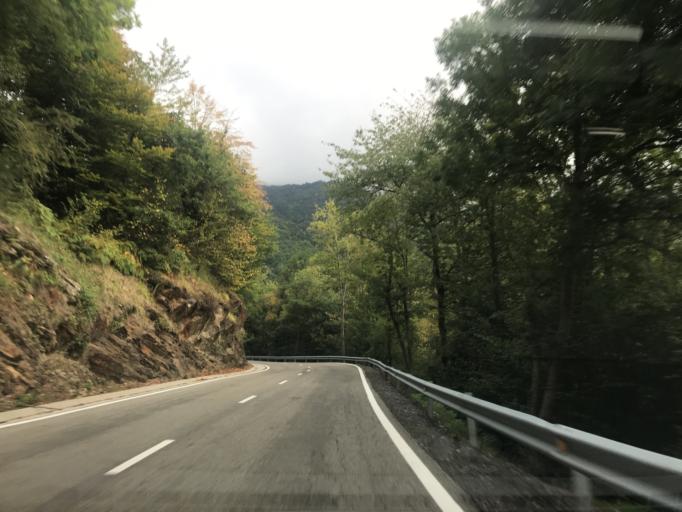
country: ES
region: Catalonia
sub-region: Provincia de Lleida
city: Les
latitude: 42.7804
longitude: 0.6798
